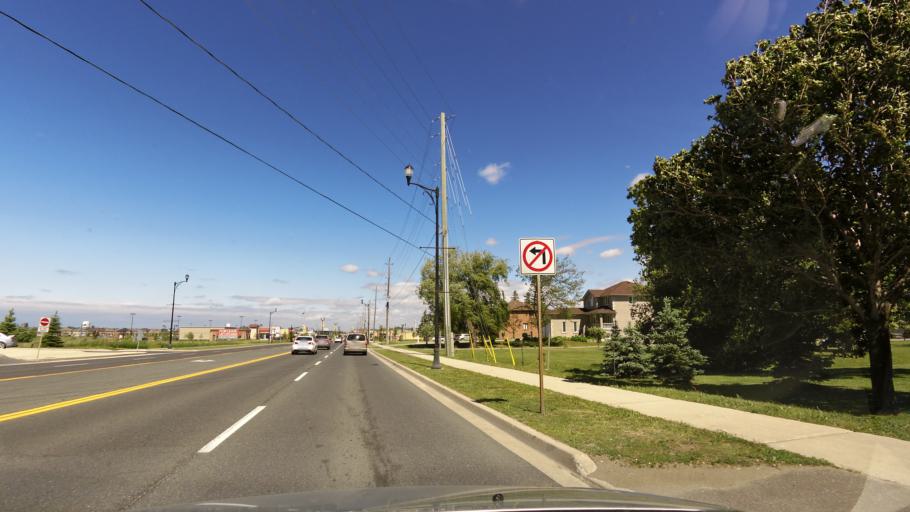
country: CA
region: Ontario
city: Bradford West Gwillimbury
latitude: 44.1071
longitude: -79.5964
